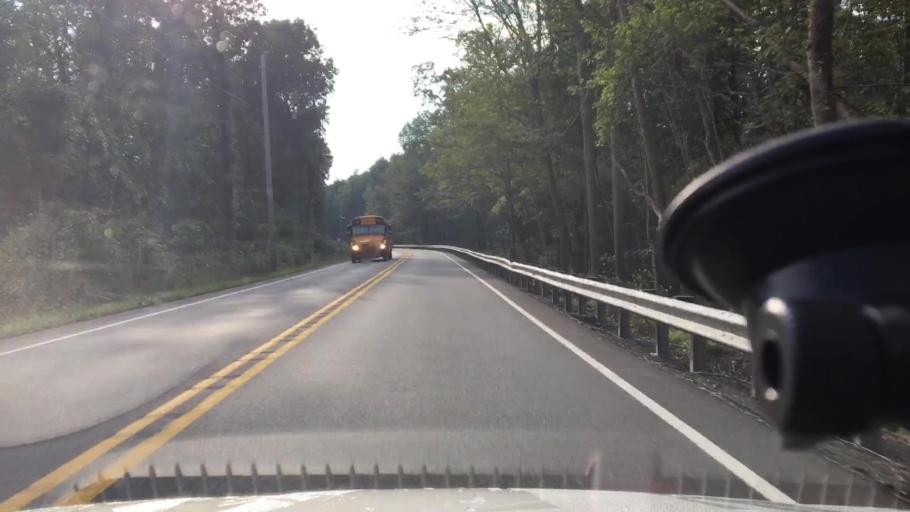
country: US
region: Pennsylvania
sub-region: Monroe County
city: Parkside
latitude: 41.1265
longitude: -75.2950
